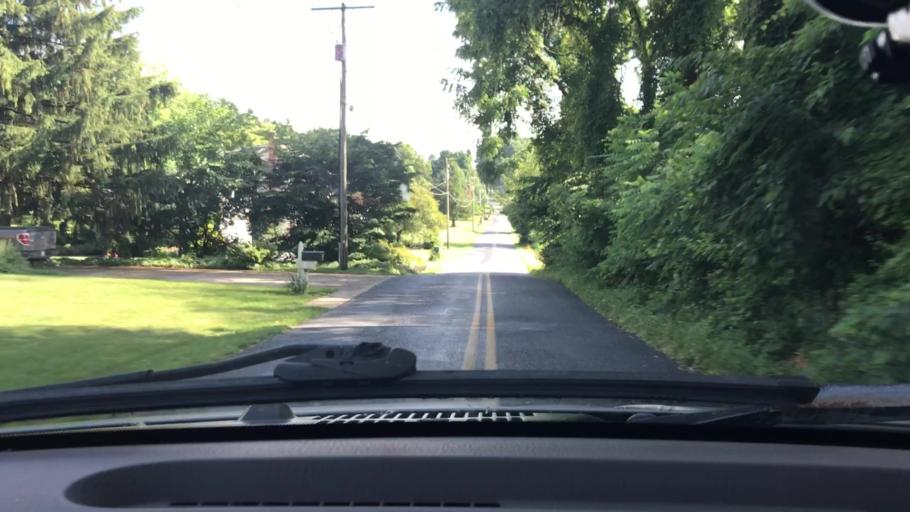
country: US
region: Pennsylvania
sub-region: Lancaster County
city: Elizabethtown
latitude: 40.1760
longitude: -76.6065
